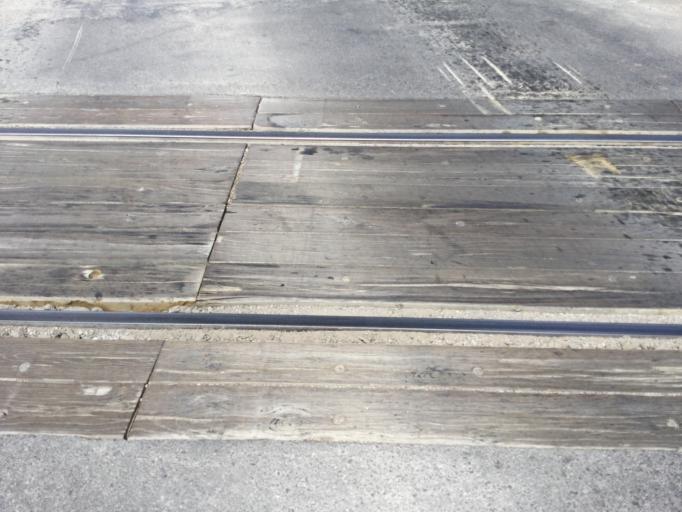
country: US
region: Kansas
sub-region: Neosho County
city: Chanute
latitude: 37.6975
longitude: -95.4527
